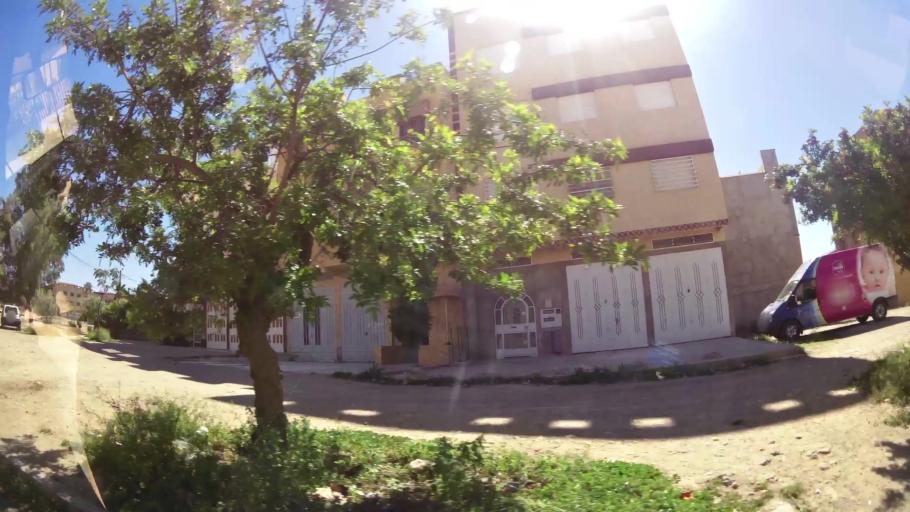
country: MA
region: Oriental
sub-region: Oujda-Angad
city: Oujda
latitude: 34.6628
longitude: -1.8704
